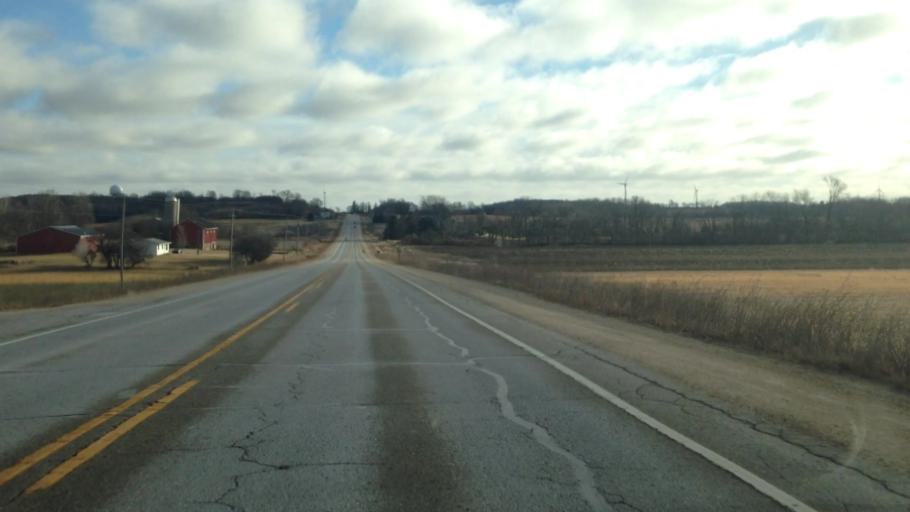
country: US
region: Wisconsin
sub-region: Dodge County
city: Mayville
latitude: 43.4428
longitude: -88.5107
